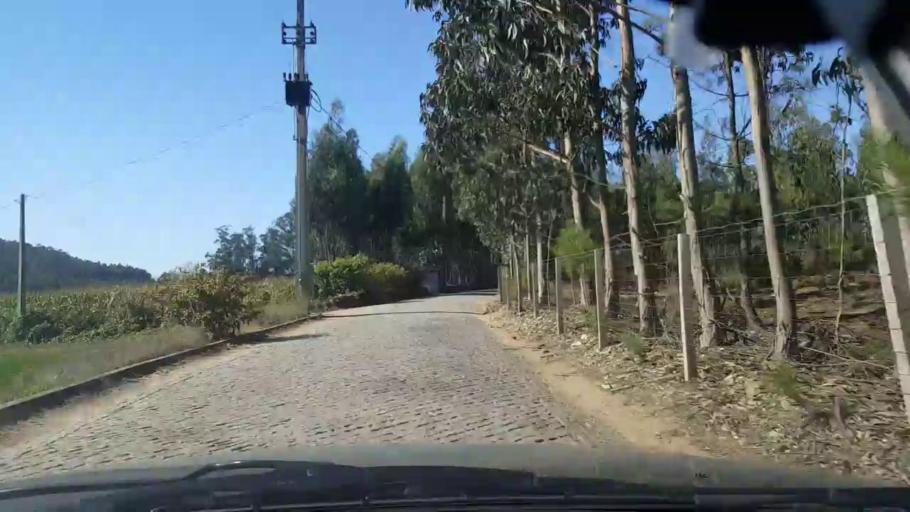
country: PT
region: Braga
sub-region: Vila Nova de Famalicao
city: Ribeirao
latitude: 41.3911
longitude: -8.6362
